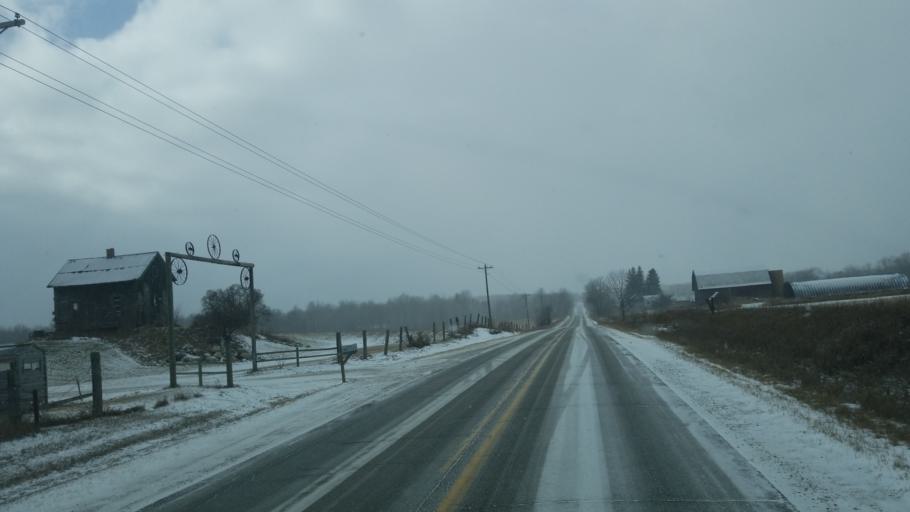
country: US
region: Michigan
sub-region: Osceola County
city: Evart
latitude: 44.0303
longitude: -85.2115
